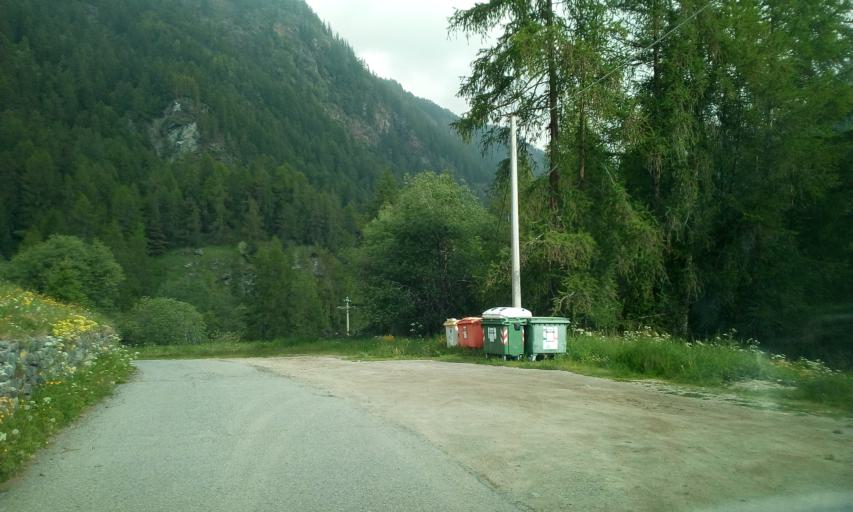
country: IT
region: Aosta Valley
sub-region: Valle d'Aosta
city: Torgnon
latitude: 45.8190
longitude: 7.5776
